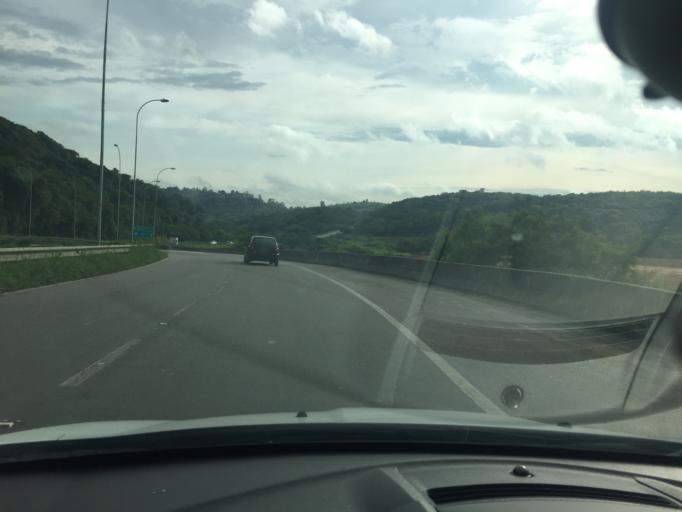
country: BR
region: Sao Paulo
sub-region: Campo Limpo Paulista
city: Campo Limpo Paulista
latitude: -23.1978
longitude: -46.7957
